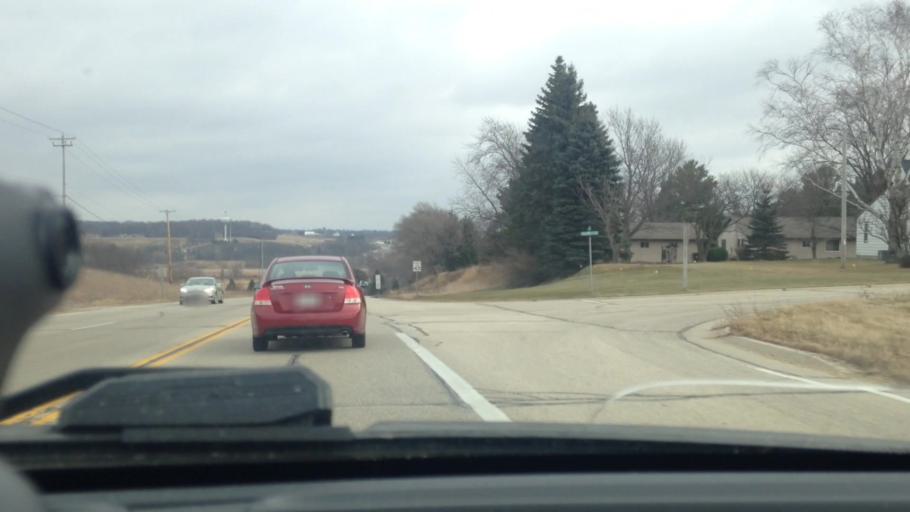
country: US
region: Wisconsin
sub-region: Washington County
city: Hartford
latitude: 43.4216
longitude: -88.3566
